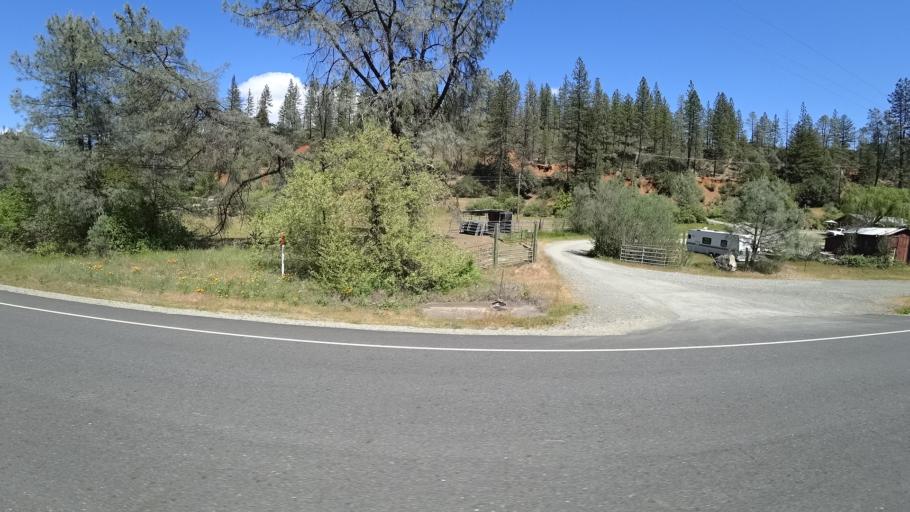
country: US
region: California
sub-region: Trinity County
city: Weaverville
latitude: 40.7276
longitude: -123.0552
